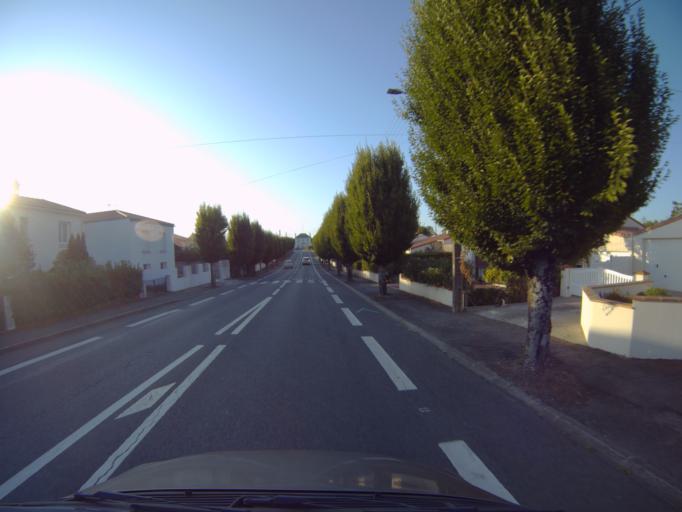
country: FR
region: Pays de la Loire
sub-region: Departement de la Vendee
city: Montaigu
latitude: 46.9825
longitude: -1.3144
